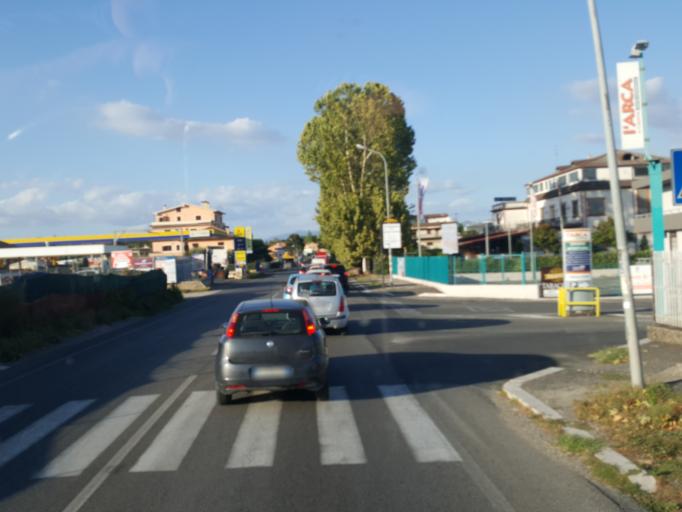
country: IT
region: Latium
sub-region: Citta metropolitana di Roma Capitale
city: Bivio di Capanelle
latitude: 42.1174
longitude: 12.5888
